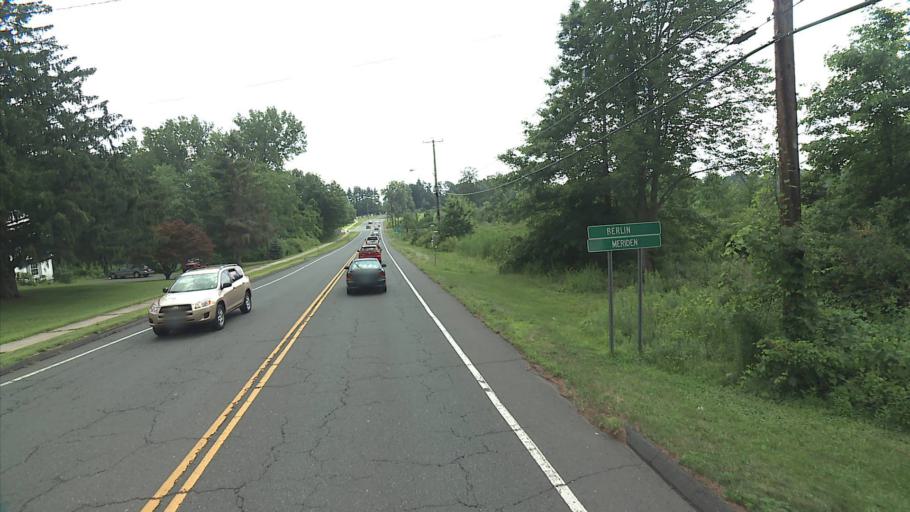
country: US
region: Connecticut
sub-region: Hartford County
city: Newington
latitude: 41.6952
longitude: -72.7331
